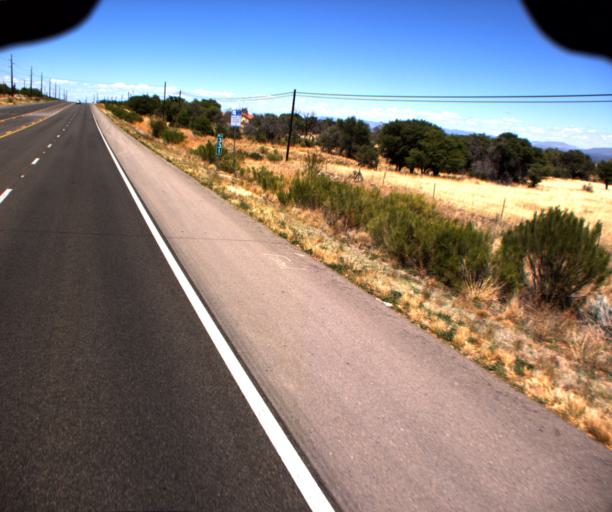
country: US
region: Arizona
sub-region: Cochise County
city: Sierra Vista Southeast
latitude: 31.4174
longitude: -110.2407
